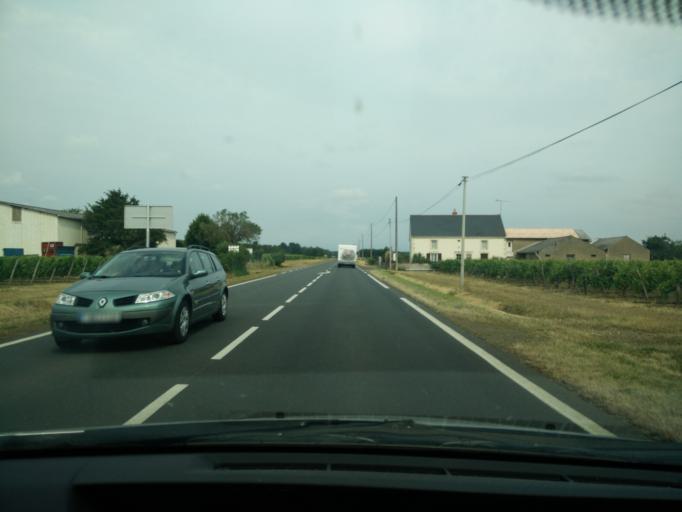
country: FR
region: Pays de la Loire
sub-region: Departement de Maine-et-Loire
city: Montreuil-Bellay
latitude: 47.1438
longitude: -0.1647
